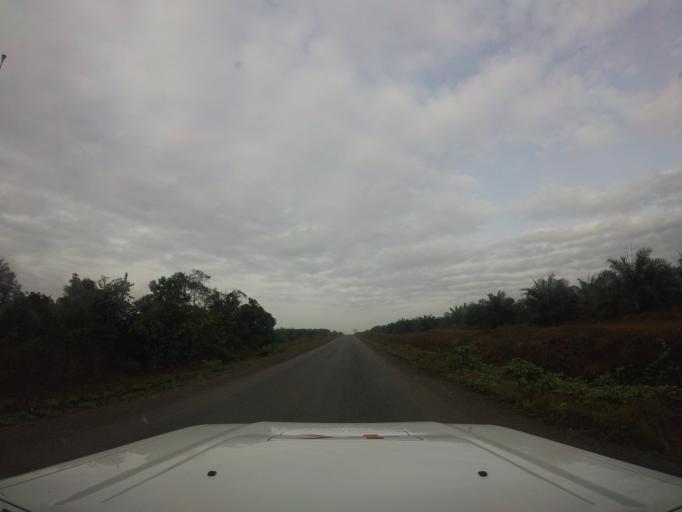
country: LR
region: Bomi
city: Tubmanburg
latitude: 6.7287
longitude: -11.0258
